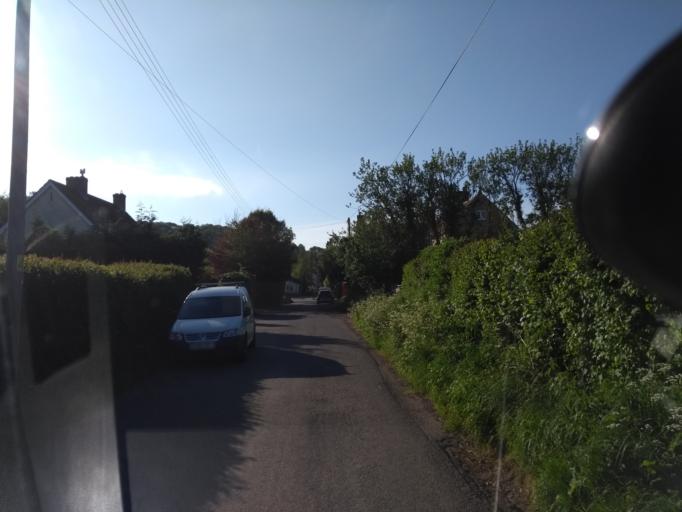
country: GB
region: England
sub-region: Somerset
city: Creech Saint Michael
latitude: 50.9955
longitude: -3.0535
